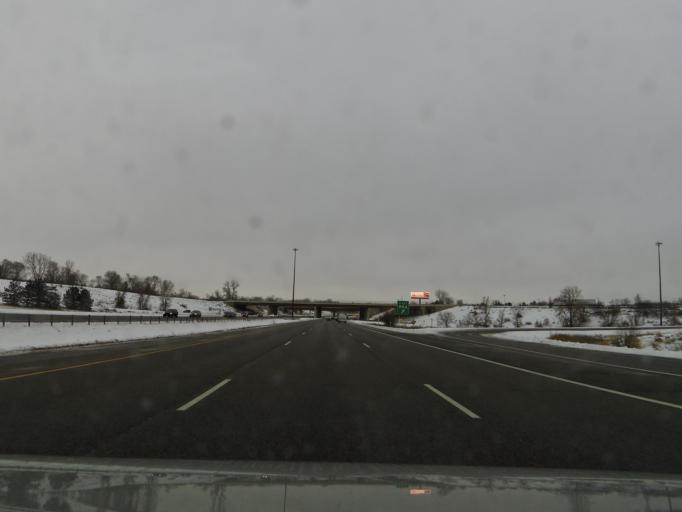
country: US
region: Minnesota
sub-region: Dakota County
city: Mendota Heights
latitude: 44.8621
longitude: -93.1457
